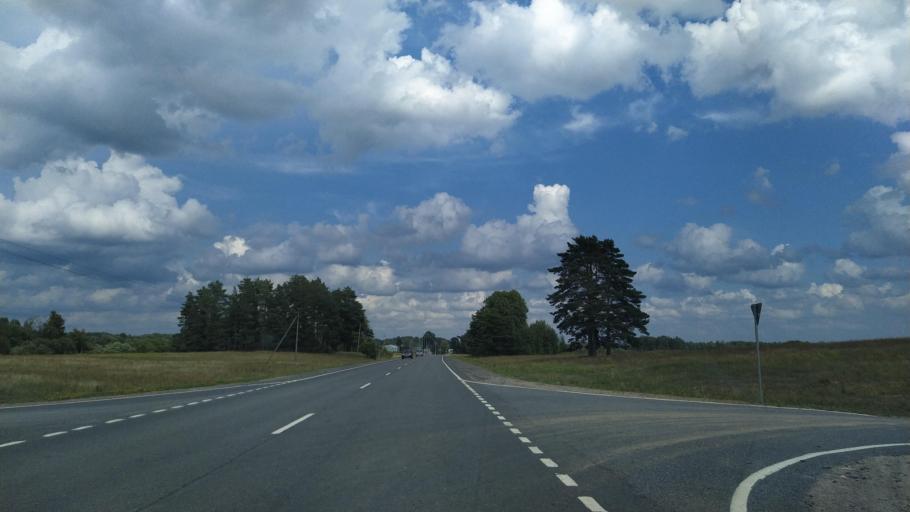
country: RU
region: Novgorod
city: Sol'tsy
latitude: 58.0992
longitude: 30.1887
